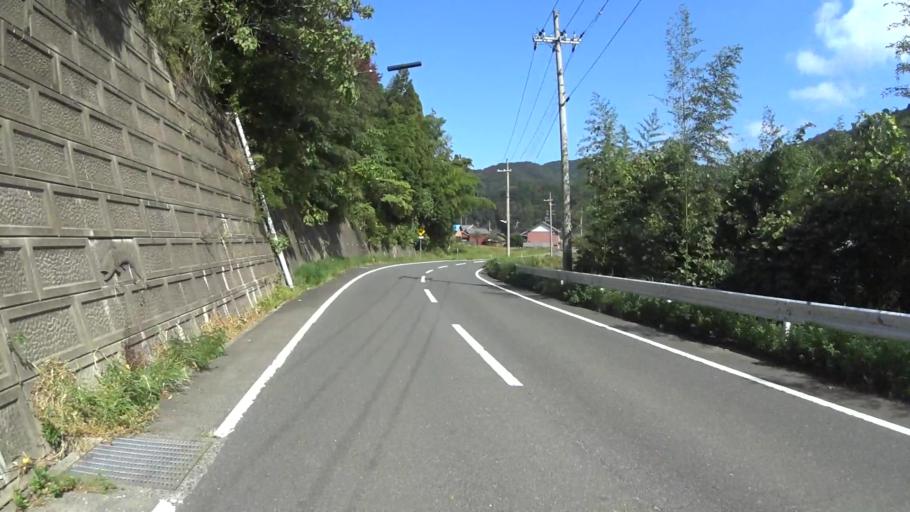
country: JP
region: Kyoto
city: Miyazu
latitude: 35.7128
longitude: 135.2498
